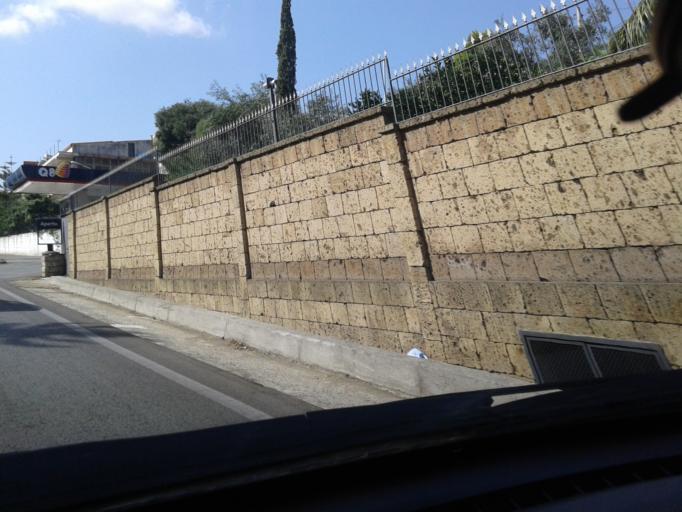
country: IT
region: Sicily
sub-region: Palermo
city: Monreale
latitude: 38.0882
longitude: 13.3026
